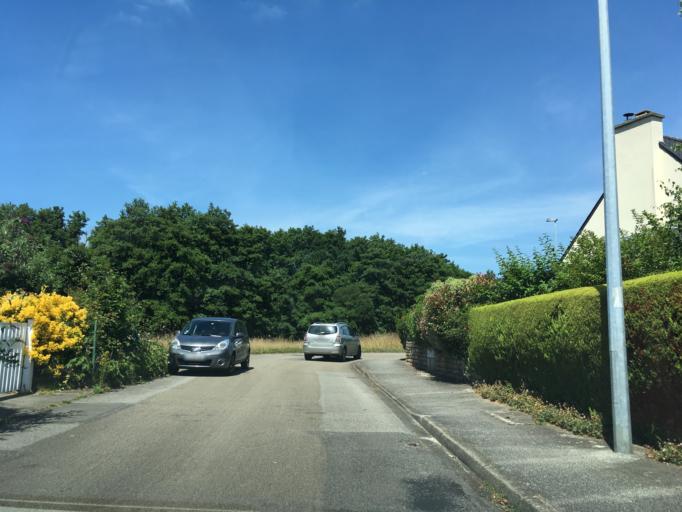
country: FR
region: Brittany
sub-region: Departement du Finistere
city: Quimper
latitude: 48.0051
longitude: -4.1144
